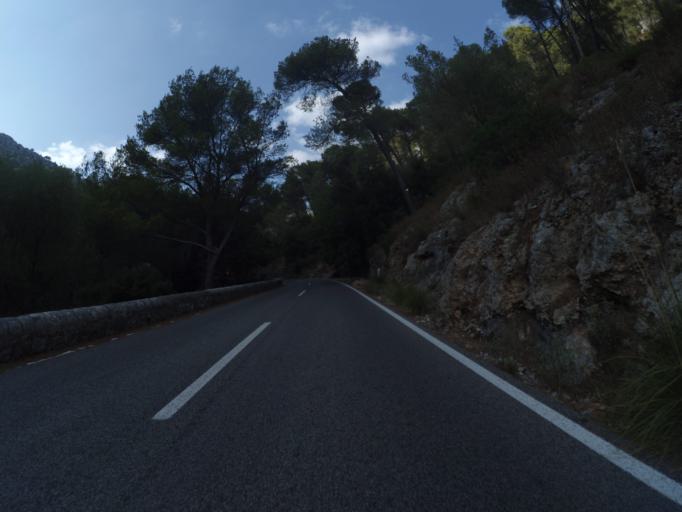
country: ES
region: Balearic Islands
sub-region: Illes Balears
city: Selva
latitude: 39.7814
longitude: 2.8968
